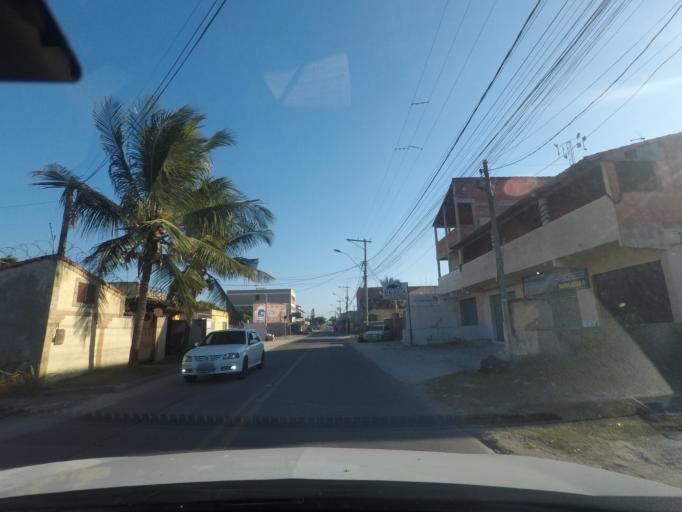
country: BR
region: Rio de Janeiro
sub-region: Marica
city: Marica
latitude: -22.9630
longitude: -42.9424
